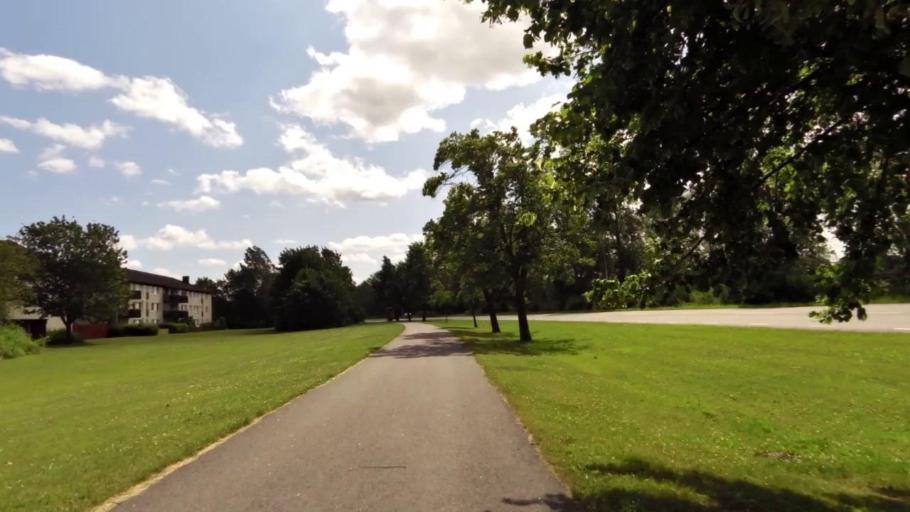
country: SE
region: OEstergoetland
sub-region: Linkopings Kommun
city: Malmslatt
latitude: 58.4306
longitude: 15.5677
